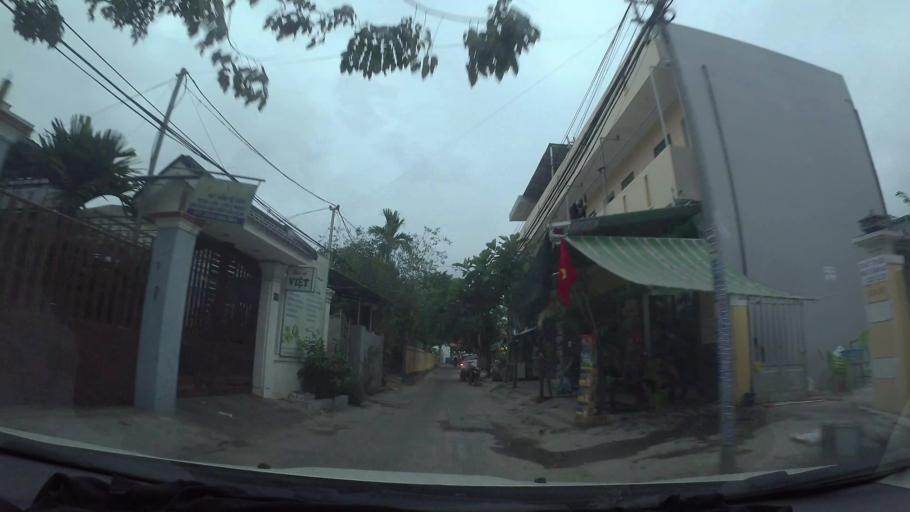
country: VN
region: Da Nang
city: Lien Chieu
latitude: 16.0854
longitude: 108.1527
